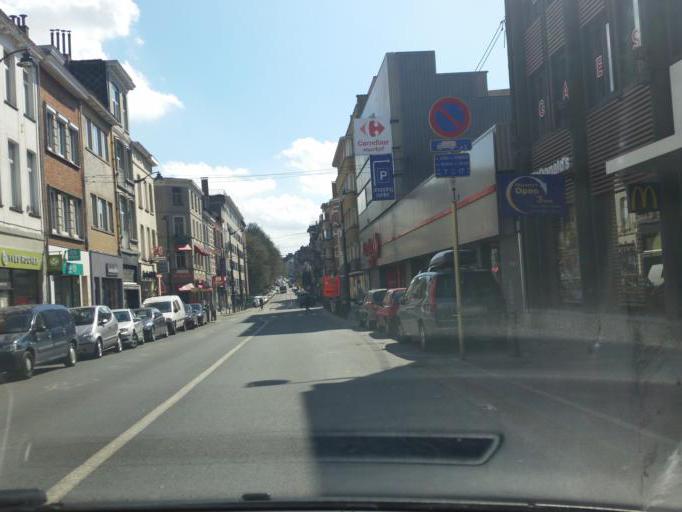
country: BE
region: Brussels Capital
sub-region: Bruxelles-Capitale
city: Brussels
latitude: 50.8155
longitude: 4.3671
